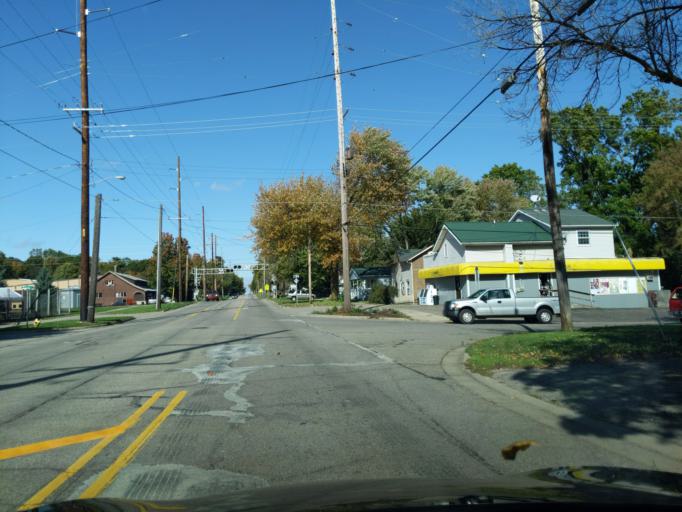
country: US
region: Michigan
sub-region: Eaton County
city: Charlotte
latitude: 42.5699
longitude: -84.8359
